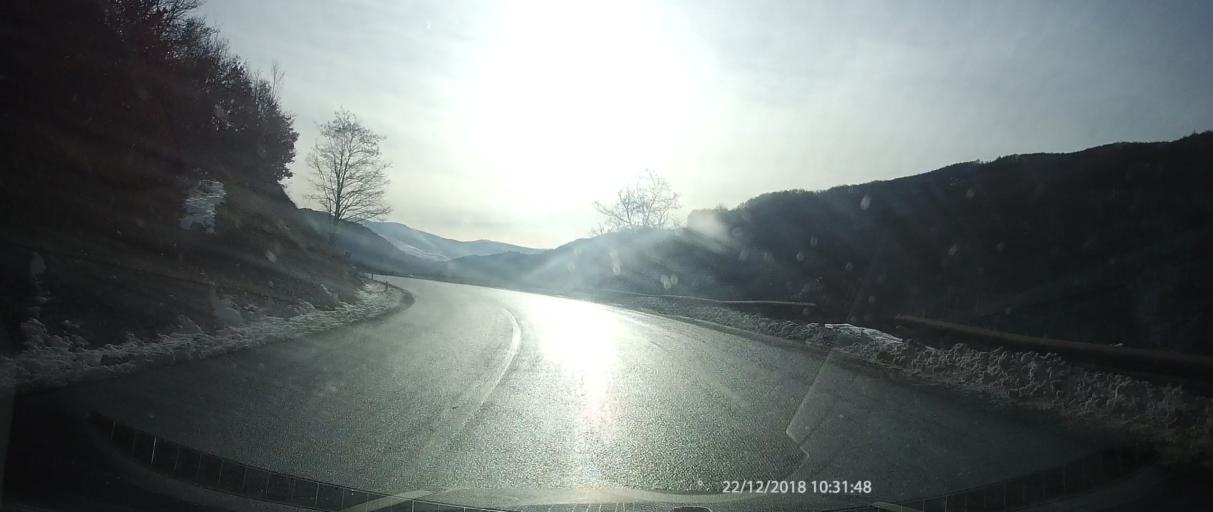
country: MK
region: Kriva Palanka
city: Kriva Palanka
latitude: 42.2221
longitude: 22.4269
